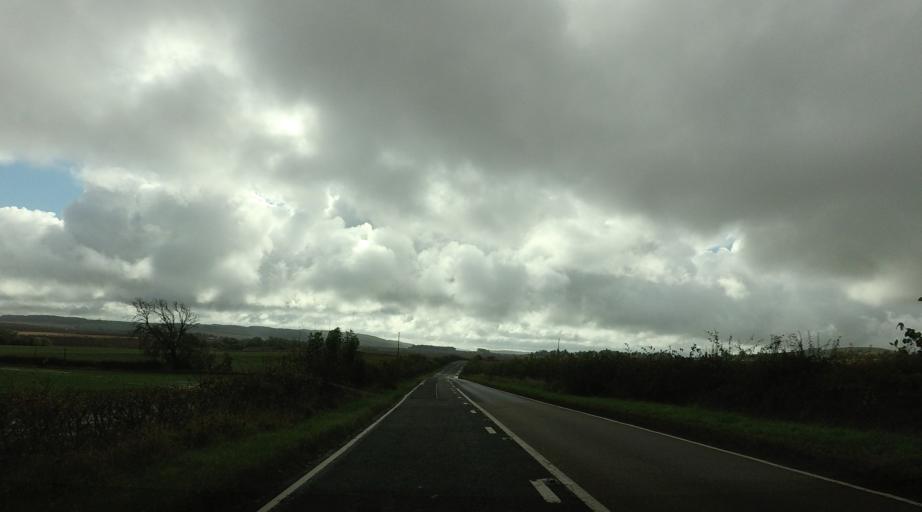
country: GB
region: Scotland
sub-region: Fife
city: Balmullo
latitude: 56.3706
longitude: -2.9318
